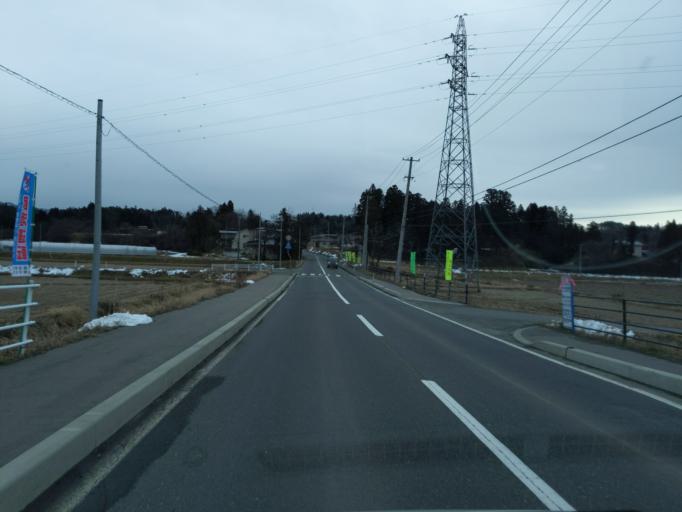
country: JP
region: Iwate
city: Mizusawa
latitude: 39.1589
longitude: 141.2039
